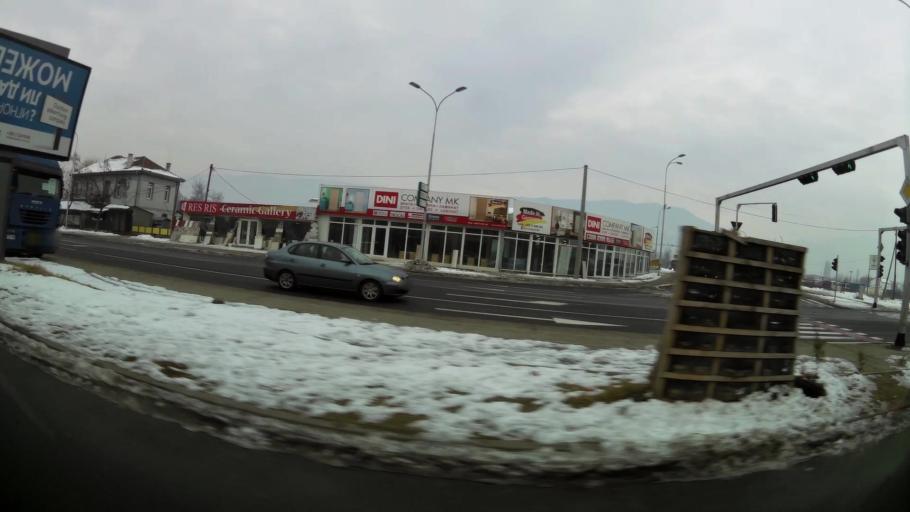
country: MK
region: Saraj
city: Saraj
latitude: 42.0070
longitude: 21.3331
